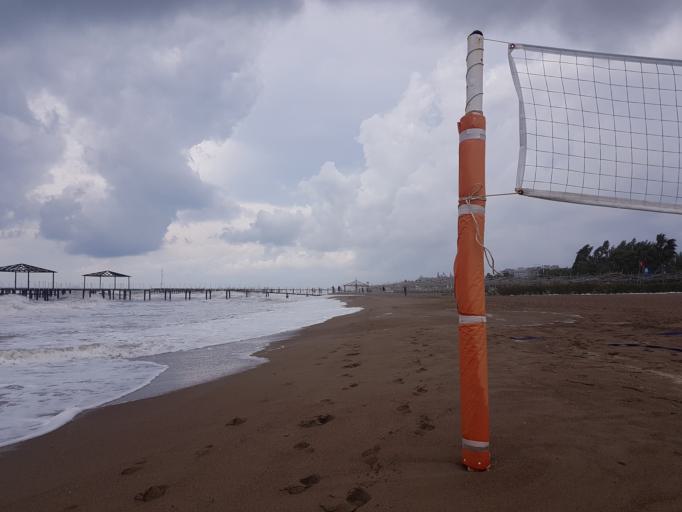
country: TR
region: Antalya
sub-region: Serik
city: Kumkoey
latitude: 36.8533
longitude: 30.8922
